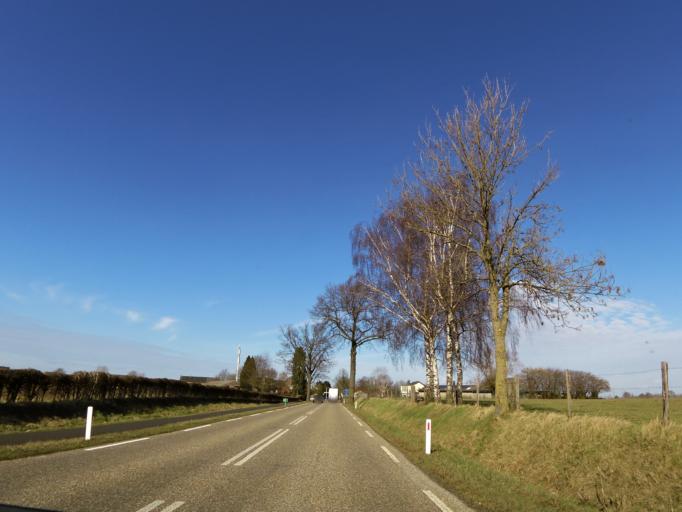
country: NL
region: Limburg
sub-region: Eijsden-Margraten
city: Margraten
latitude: 50.7919
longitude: 5.8325
